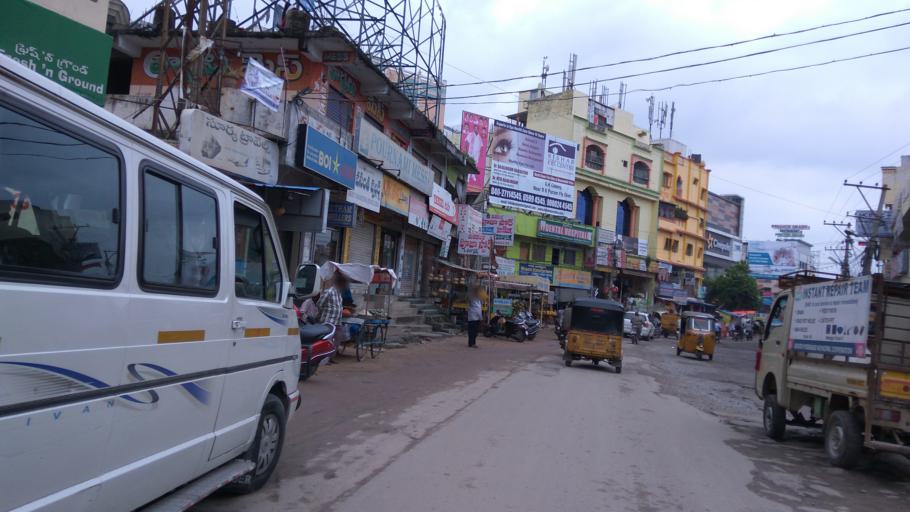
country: IN
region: Telangana
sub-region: Hyderabad
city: Malkajgiri
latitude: 17.4583
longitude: 78.5366
